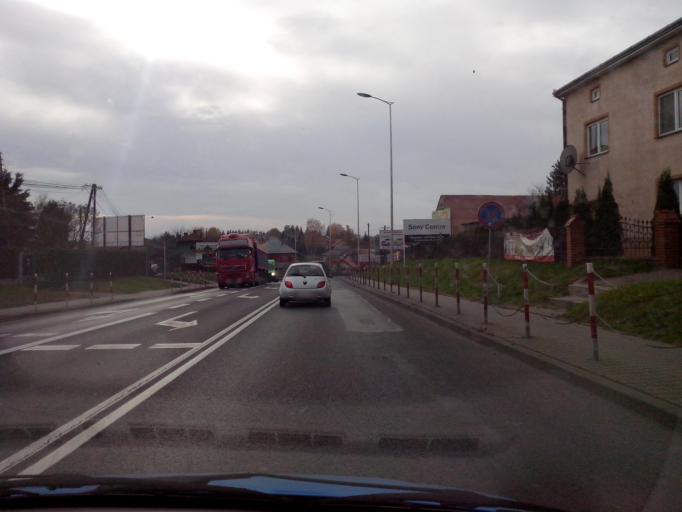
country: PL
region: Subcarpathian Voivodeship
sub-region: Powiat rzeszowski
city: Boguchwala
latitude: 50.0058
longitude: 21.9600
